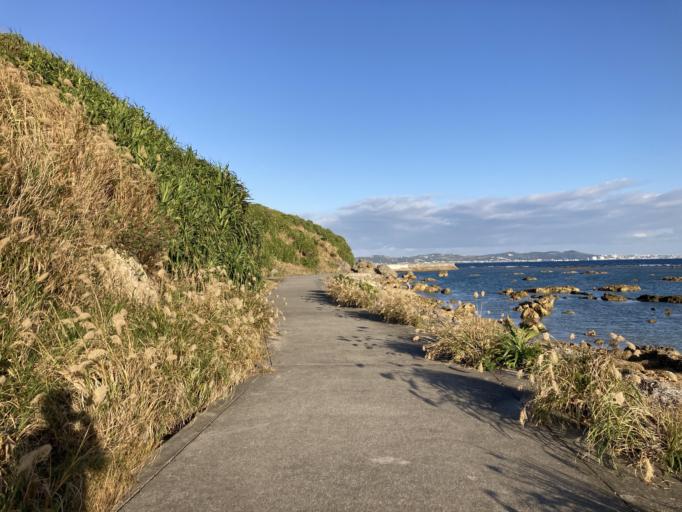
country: JP
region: Okinawa
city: Ginowan
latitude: 26.1885
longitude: 127.8224
